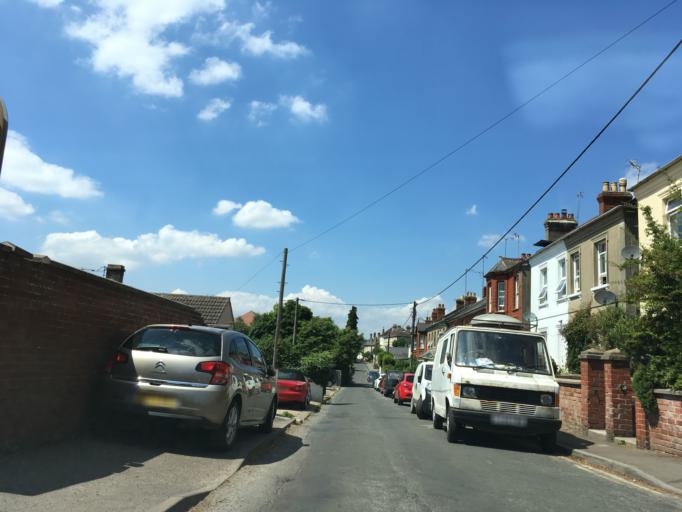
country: GB
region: England
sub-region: Gloucestershire
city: Stroud
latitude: 51.7426
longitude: -2.2059
